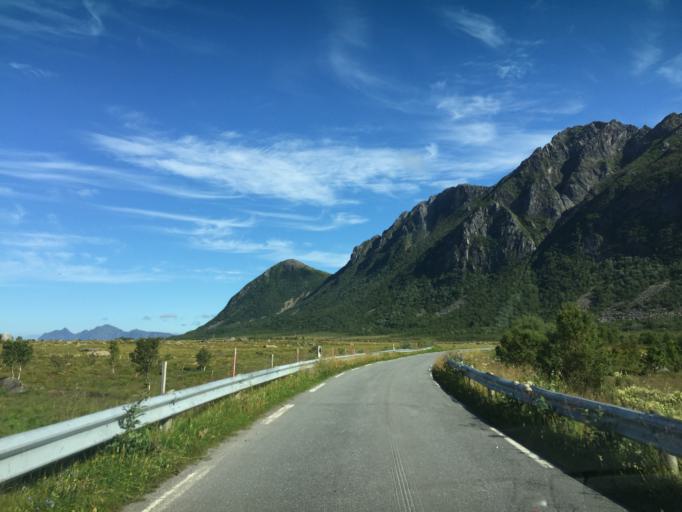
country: NO
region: Nordland
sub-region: Vagan
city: Svolvaer
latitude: 68.3981
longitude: 14.5661
